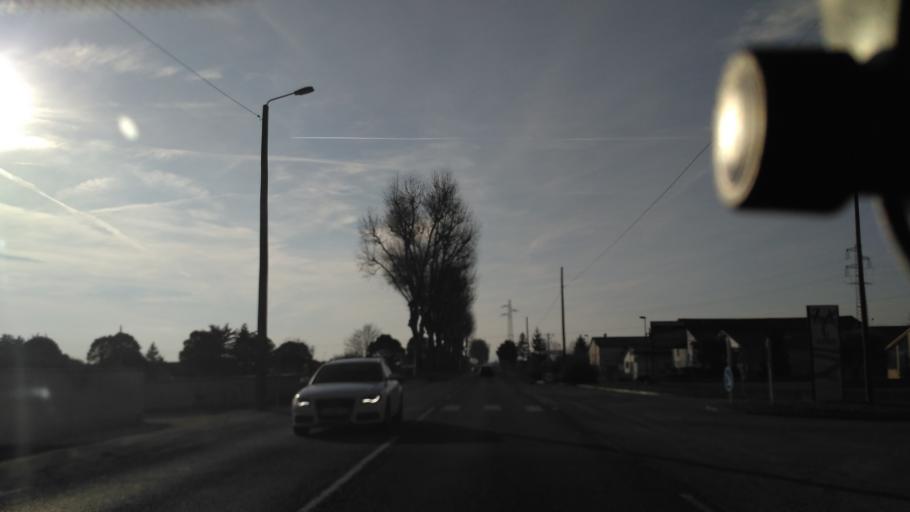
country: FR
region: Rhone-Alpes
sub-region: Departement de la Drome
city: Saint-Paul-les-Romans
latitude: 45.0689
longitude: 5.1283
